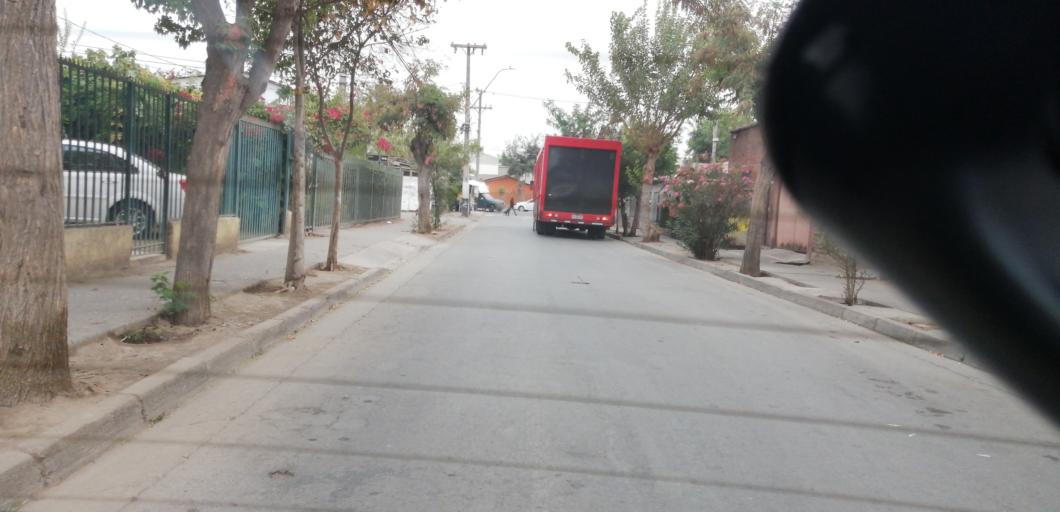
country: CL
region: Santiago Metropolitan
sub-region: Provincia de Santiago
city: Lo Prado
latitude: -33.4326
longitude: -70.7481
